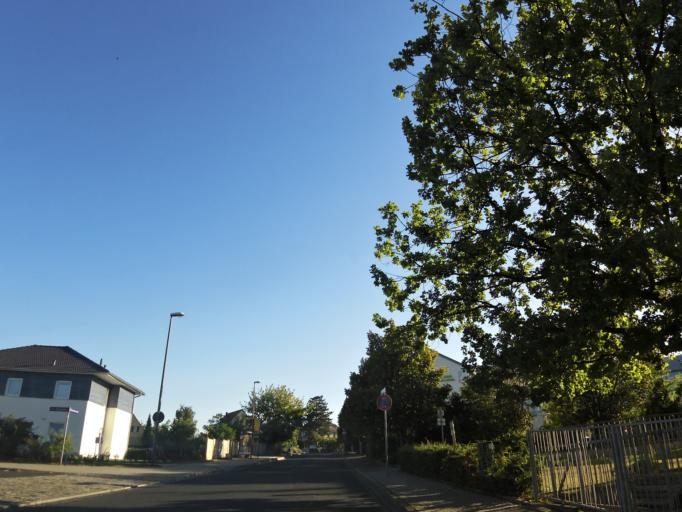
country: DE
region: Saxony
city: Dresden
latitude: 51.0088
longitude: 13.7688
